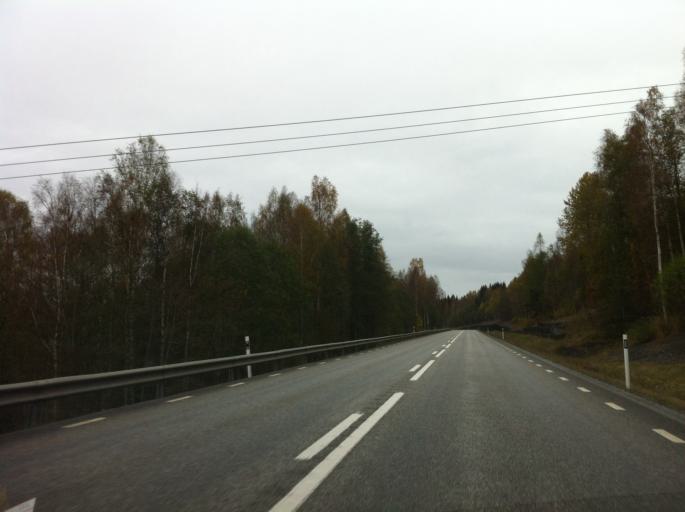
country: SE
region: OErebro
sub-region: Ljusnarsbergs Kommun
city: Kopparberg
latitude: 59.8591
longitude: 15.0599
